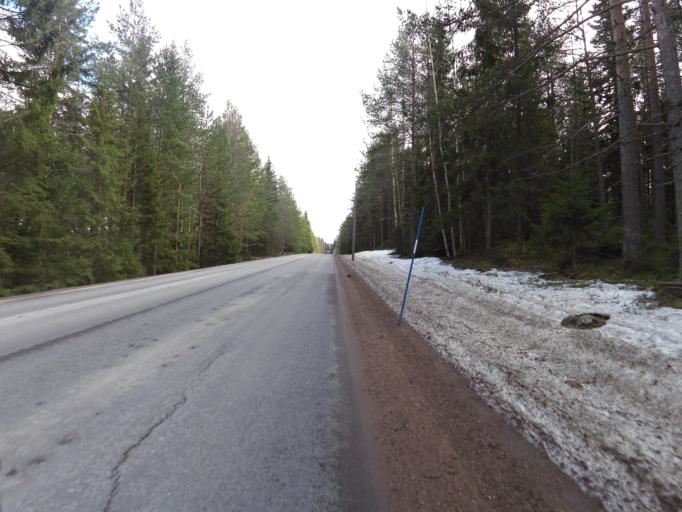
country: SE
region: Dalarna
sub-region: Hedemora Kommun
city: Brunna
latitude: 60.3157
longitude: 16.1404
